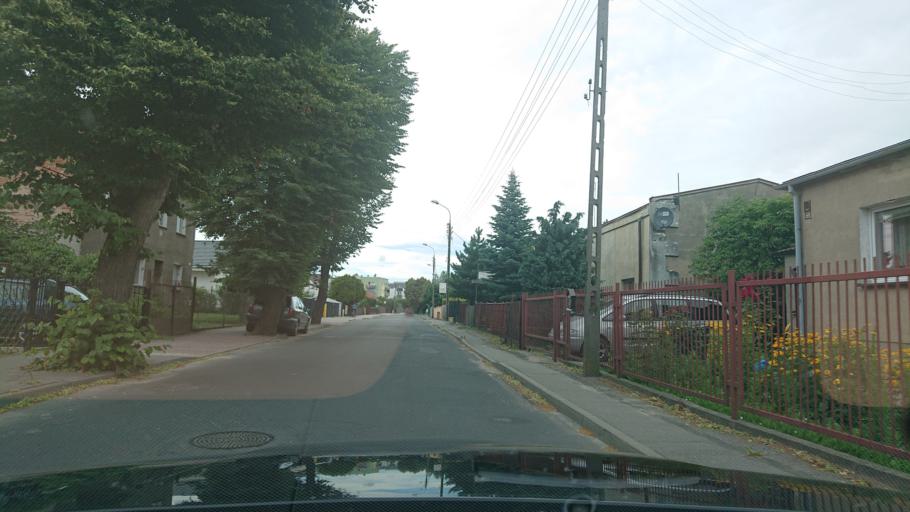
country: PL
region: Greater Poland Voivodeship
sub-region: Powiat gnieznienski
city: Gniezno
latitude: 52.5123
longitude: 17.6035
